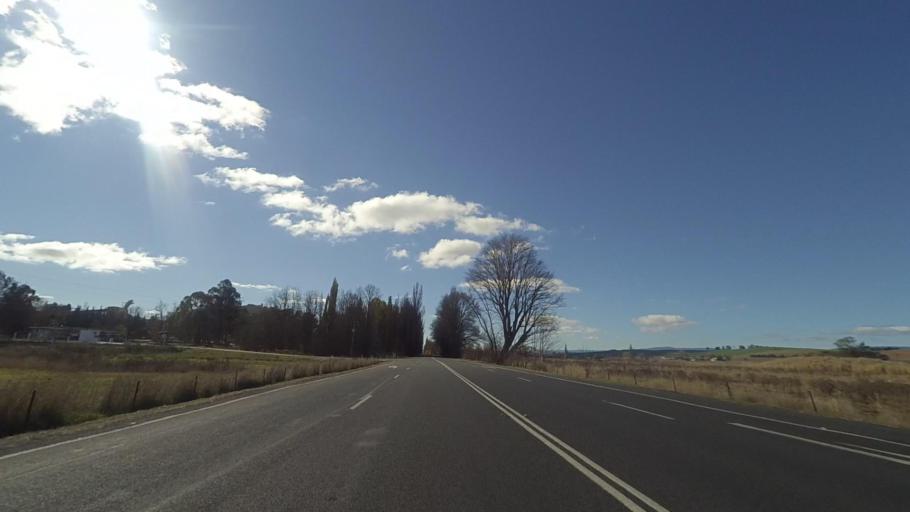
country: AU
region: New South Wales
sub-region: Bathurst Regional
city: Perthville
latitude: -33.4658
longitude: 149.5701
